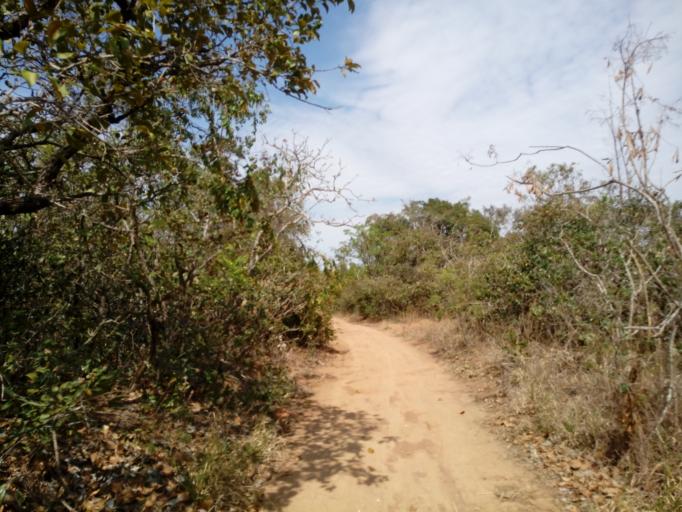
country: BR
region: Sao Paulo
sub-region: Sao Carlos
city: Sao Carlos
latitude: -21.9718
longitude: -47.8811
